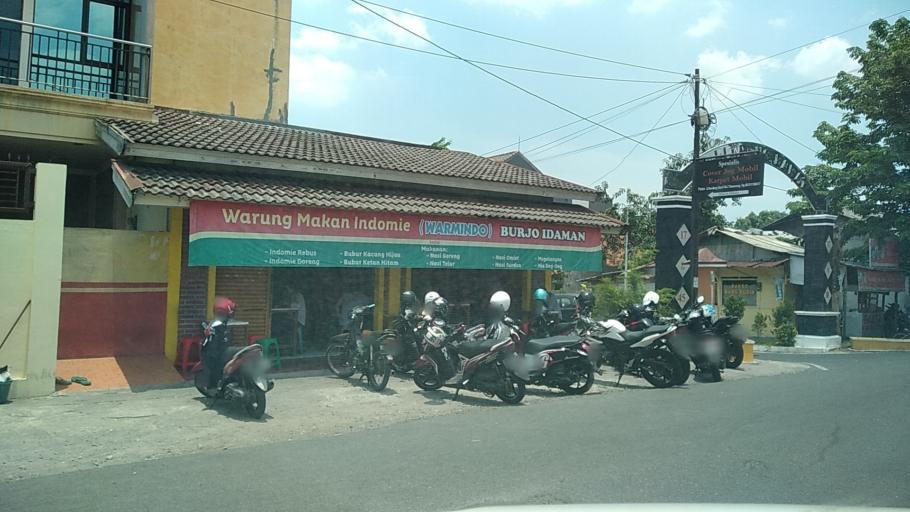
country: ID
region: Central Java
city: Semarang
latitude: -7.0159
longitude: 110.3941
